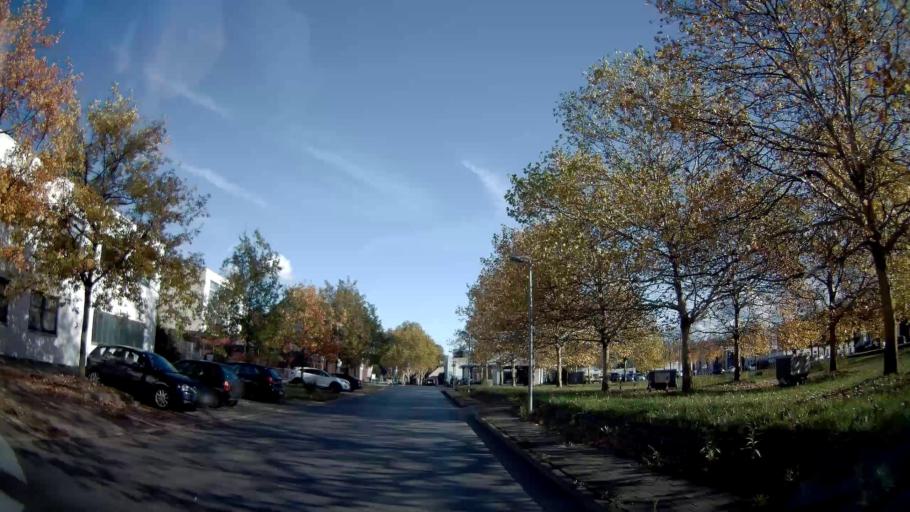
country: DE
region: North Rhine-Westphalia
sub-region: Regierungsbezirk Munster
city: Gladbeck
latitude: 51.5540
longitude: 6.9878
